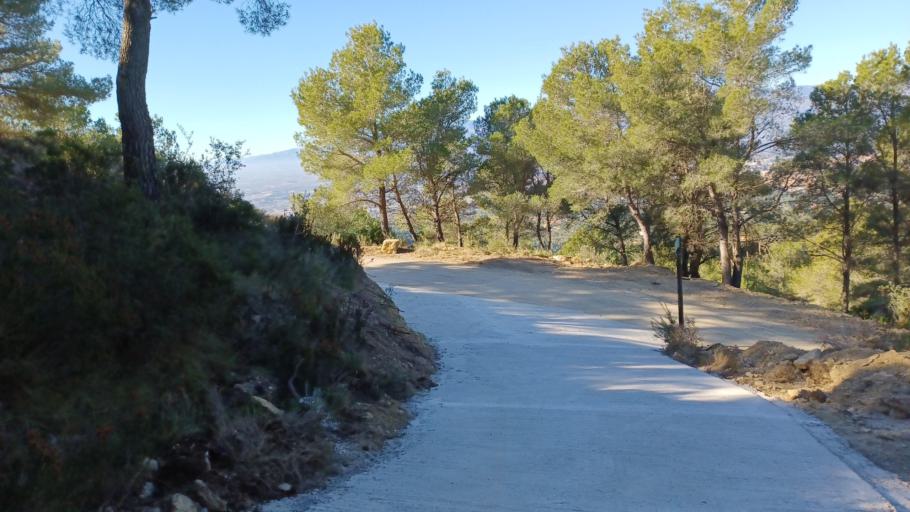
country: ES
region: Catalonia
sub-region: Provincia de Tarragona
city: Tortosa
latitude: 40.8100
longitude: 0.5659
